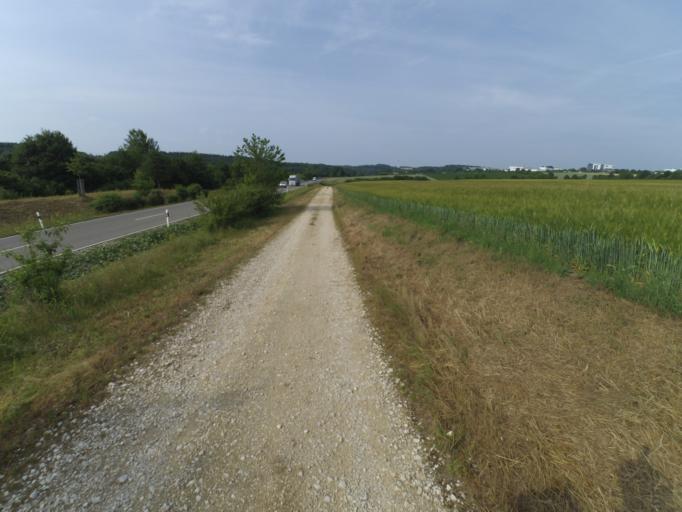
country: DE
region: Baden-Wuerttemberg
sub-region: Tuebingen Region
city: Ulm
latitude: 48.4299
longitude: 10.0014
